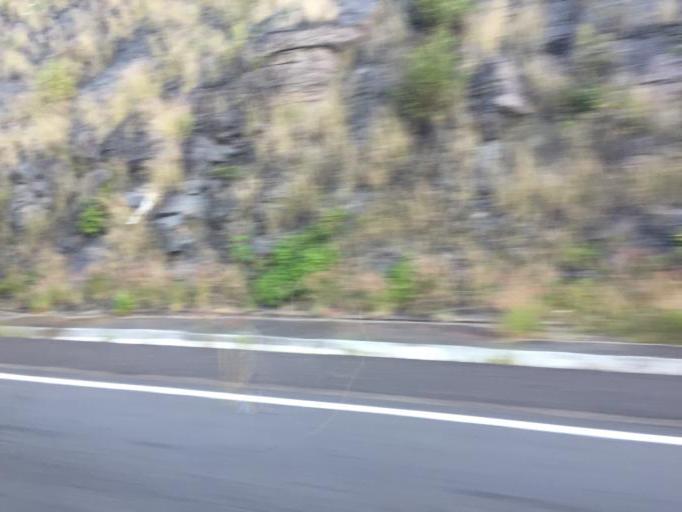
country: MX
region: Michoacan
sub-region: Zinapecuaro
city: Francisco Villa
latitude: 19.8921
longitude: -100.9049
